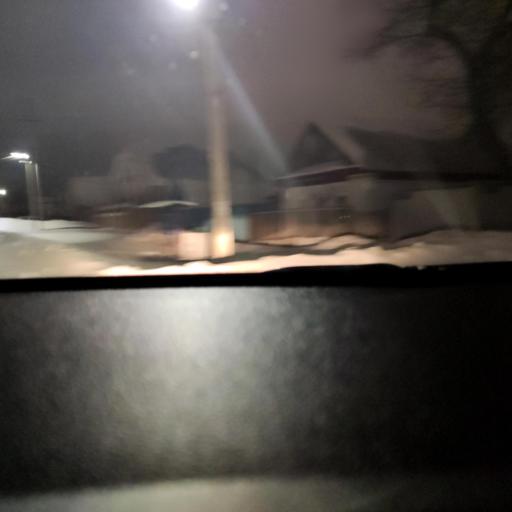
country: RU
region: Tatarstan
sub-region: Chistopol'skiy Rayon
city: Chistopol'
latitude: 55.3565
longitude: 50.6661
